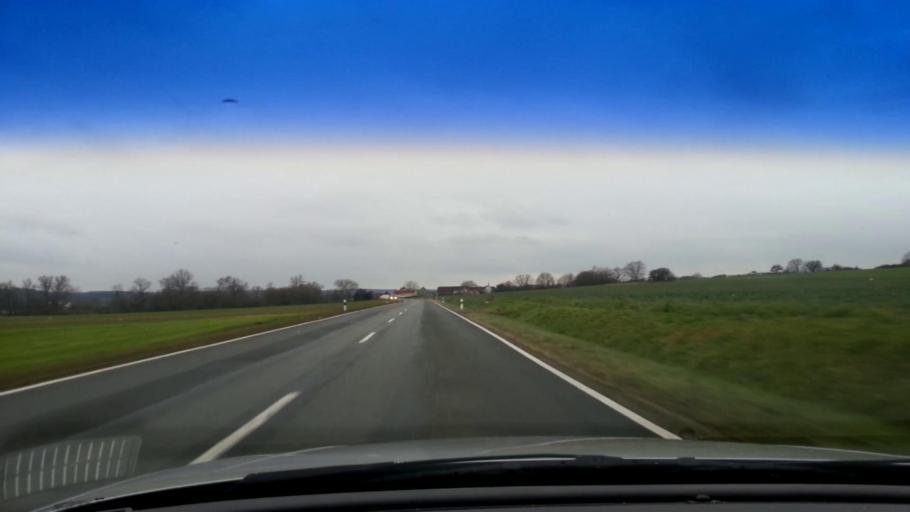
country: DE
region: Bavaria
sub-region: Upper Franconia
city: Pettstadt
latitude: 49.8271
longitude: 10.9049
